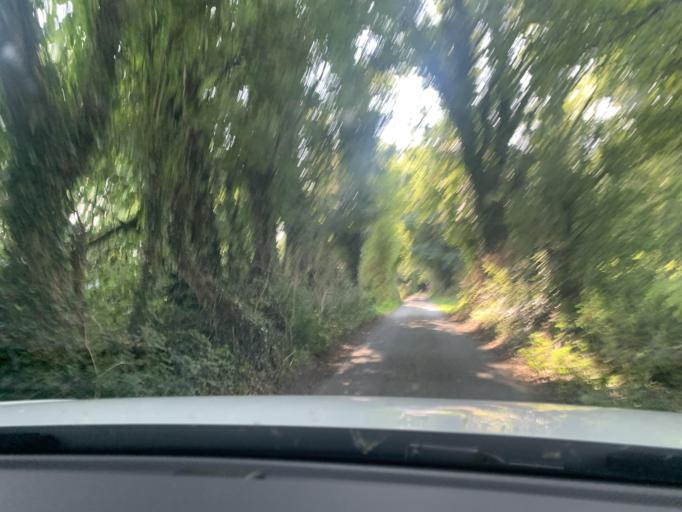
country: IE
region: Connaught
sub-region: Maigh Eo
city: Ballyhaunis
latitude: 53.7815
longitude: -8.7389
